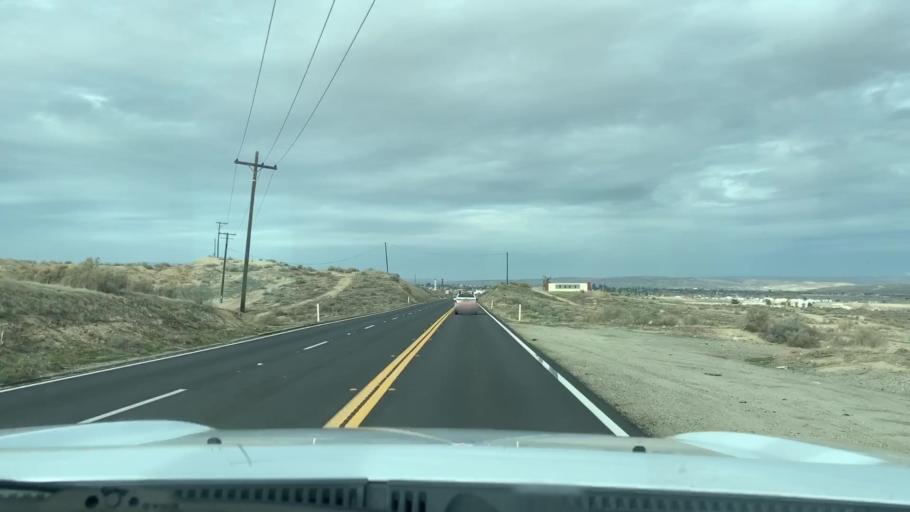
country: US
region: California
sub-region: Kern County
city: South Taft
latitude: 35.1226
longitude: -119.4367
